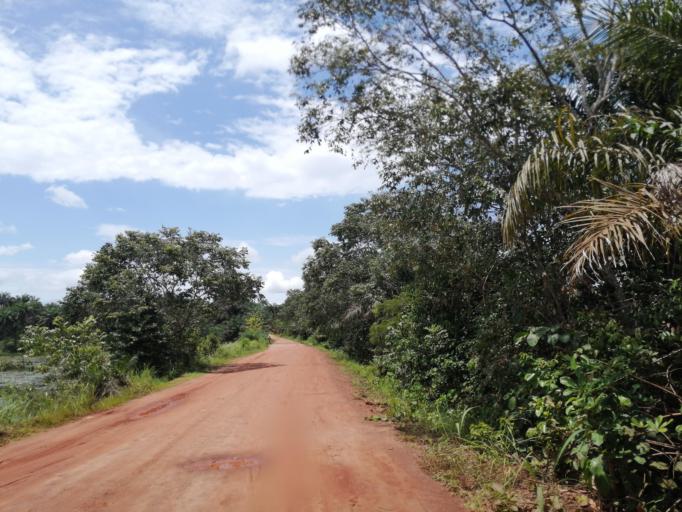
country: SL
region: Northern Province
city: Konakridee
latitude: 8.7567
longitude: -13.1423
